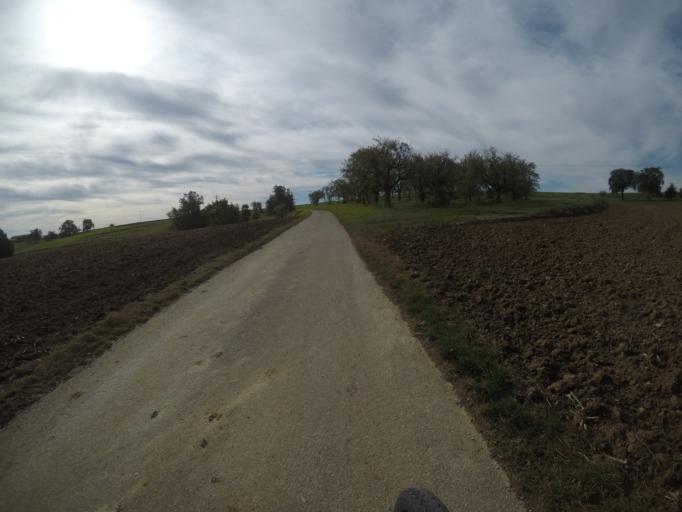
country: DE
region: Baden-Wuerttemberg
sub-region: Regierungsbezirk Stuttgart
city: Deckenpfronn
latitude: 48.6337
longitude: 8.8376
